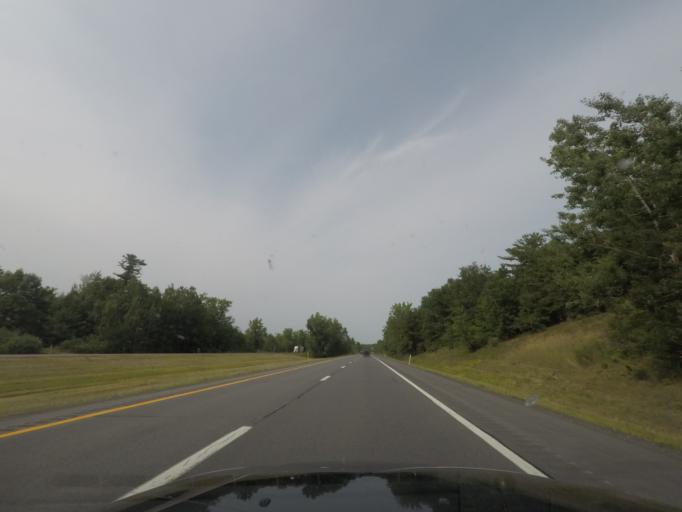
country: US
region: New York
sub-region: Essex County
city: Keeseville
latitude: 44.5200
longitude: -73.4976
